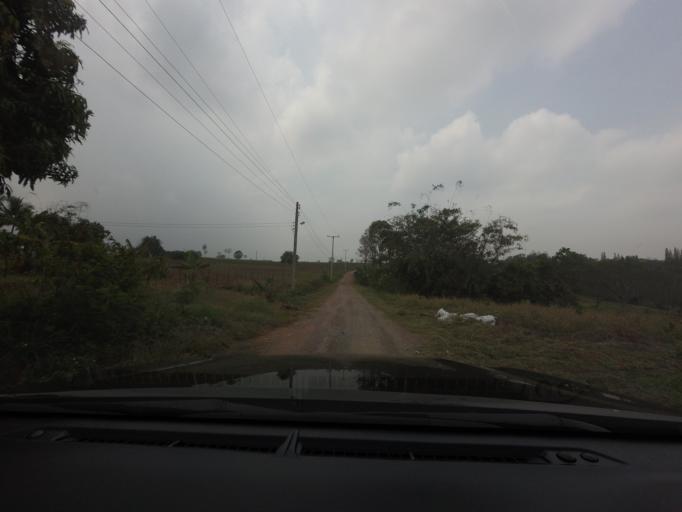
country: TH
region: Nakhon Ratchasima
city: Wang Nam Khiao
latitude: 14.4759
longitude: 101.6466
